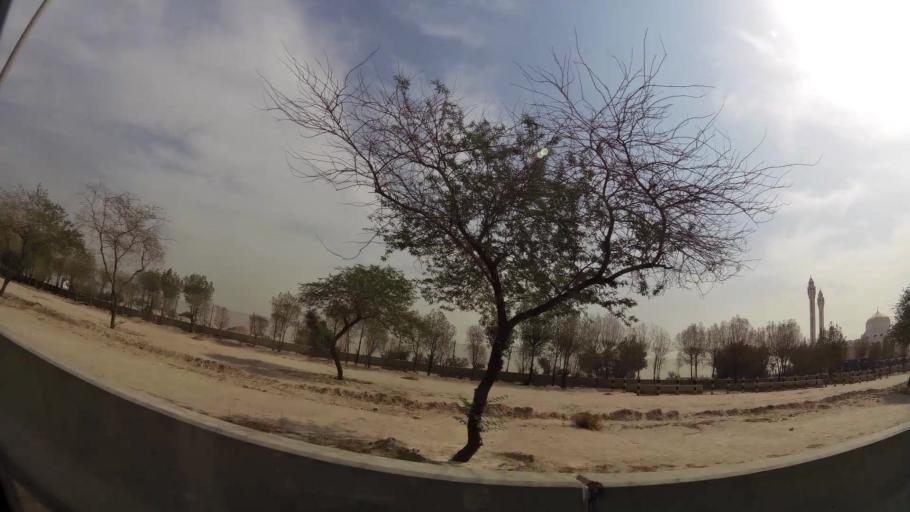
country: KW
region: Al Farwaniyah
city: Janub as Surrah
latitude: 29.2704
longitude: 47.9707
